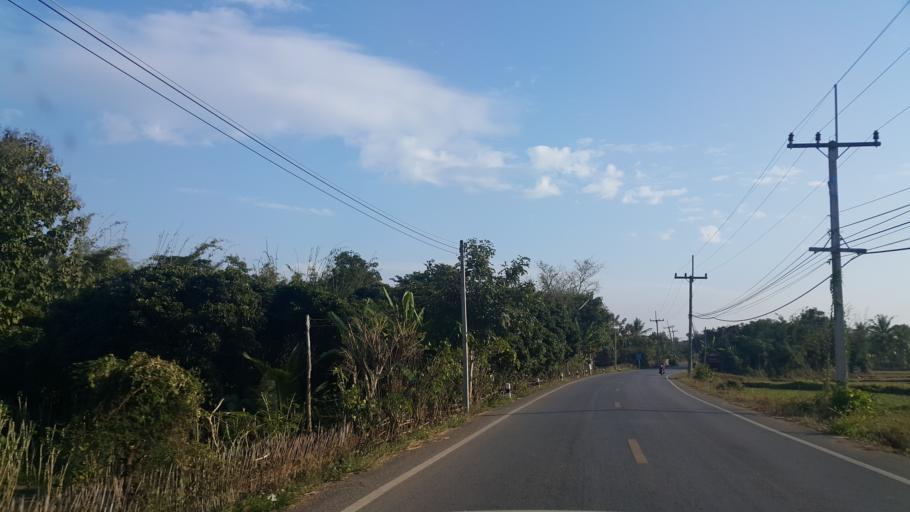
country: TH
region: Lampang
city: Soem Ngam
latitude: 18.1023
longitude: 99.3388
